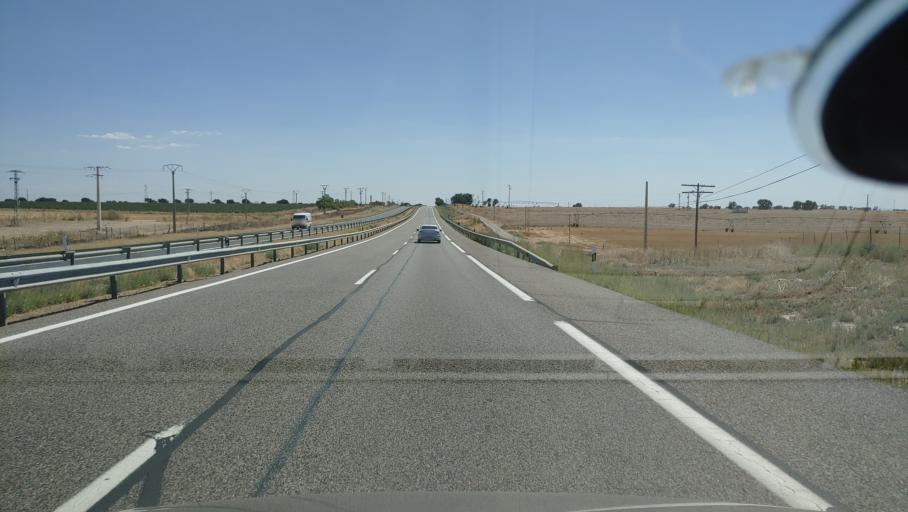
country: ES
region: Castille-La Mancha
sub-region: Provincia de Ciudad Real
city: Villarta de San Juan
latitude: 39.2026
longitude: -3.4067
